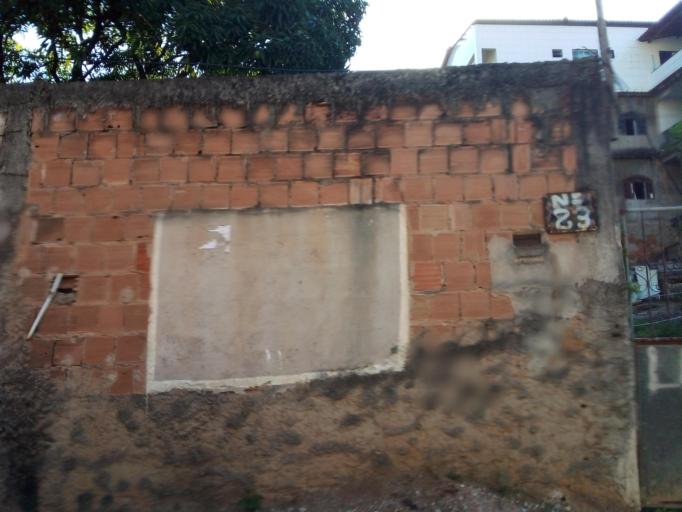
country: BR
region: Espirito Santo
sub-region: Vitoria
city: Vitoria
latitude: -20.3295
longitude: -40.3453
